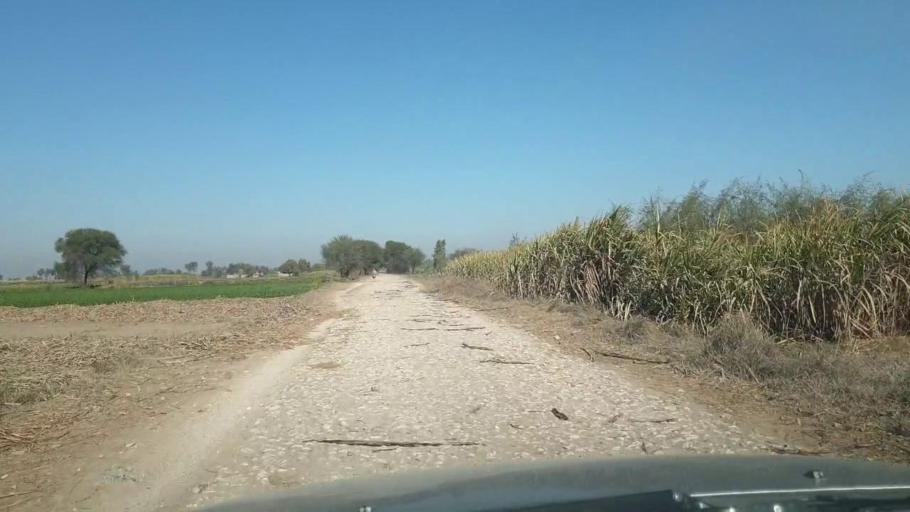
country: PK
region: Sindh
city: Ghotki
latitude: 28.0899
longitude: 69.3436
